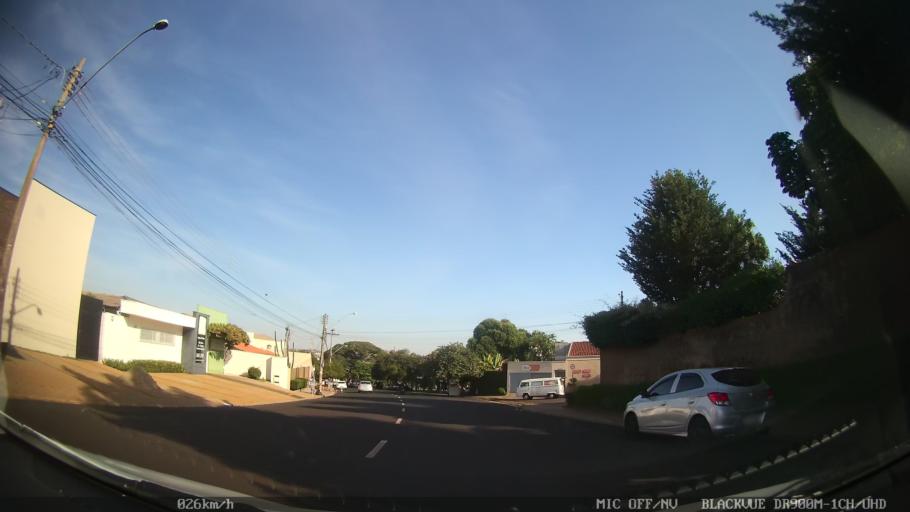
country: BR
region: Sao Paulo
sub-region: Ribeirao Preto
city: Ribeirao Preto
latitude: -21.1974
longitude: -47.8155
